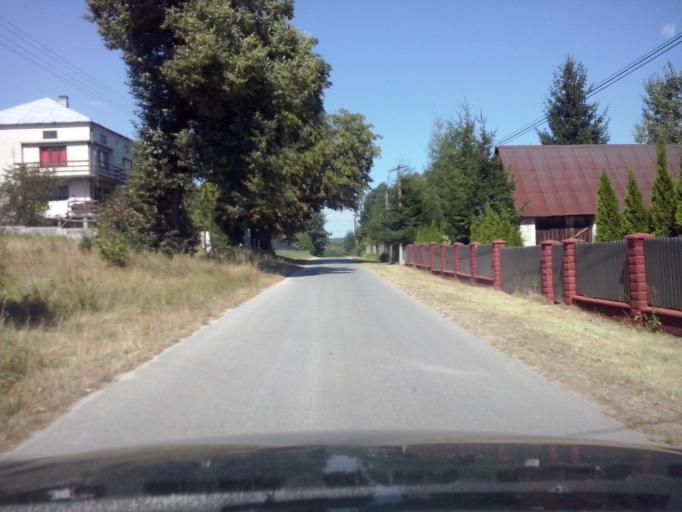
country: PL
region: Swietokrzyskie
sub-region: Powiat buski
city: Gnojno
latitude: 50.6226
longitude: 20.8809
